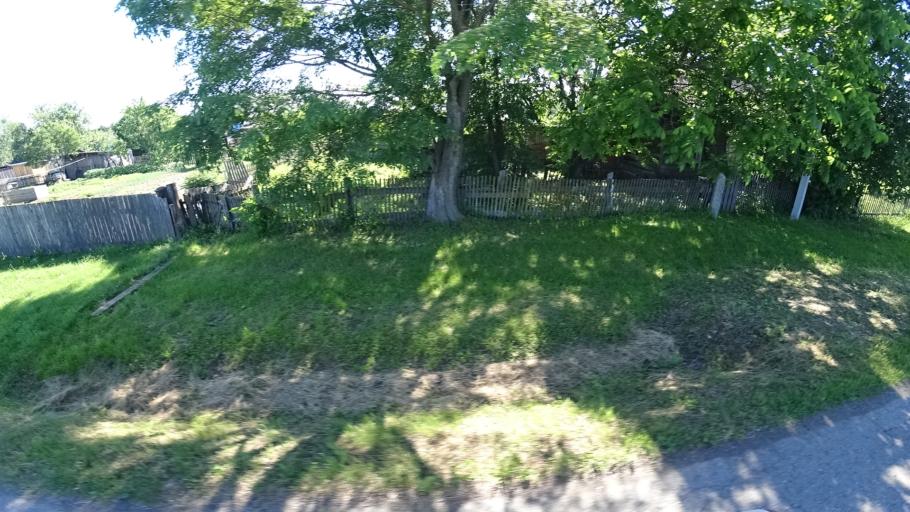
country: RU
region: Khabarovsk Krai
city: Khor
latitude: 47.8896
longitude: 134.9905
